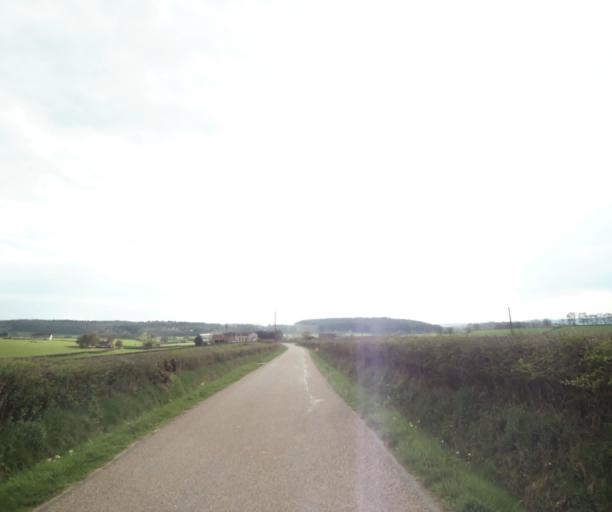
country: FR
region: Bourgogne
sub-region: Departement de Saone-et-Loire
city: Charolles
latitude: 46.5099
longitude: 4.3837
